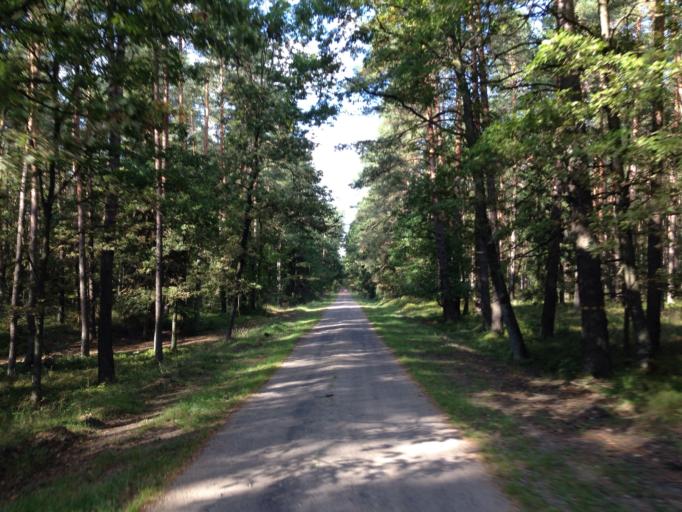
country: PL
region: Kujawsko-Pomorskie
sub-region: Powiat brodnicki
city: Gorzno
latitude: 53.1866
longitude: 19.6992
